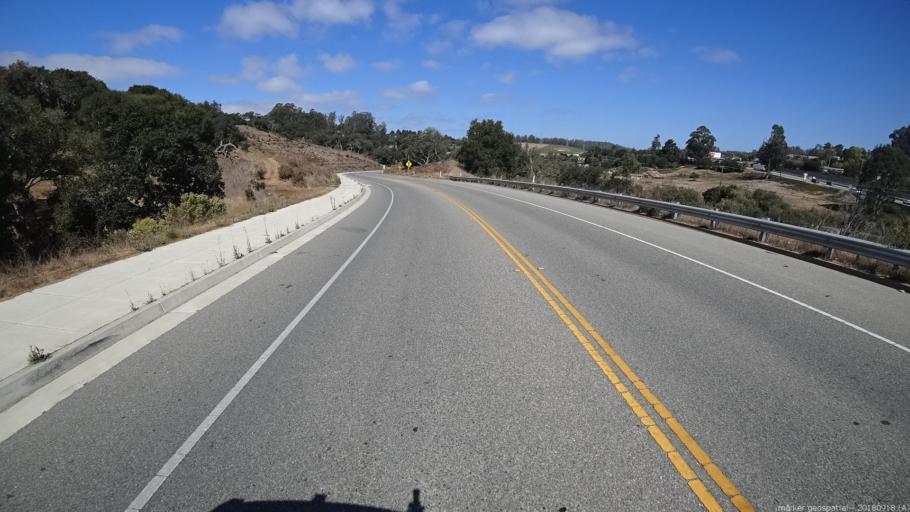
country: US
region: California
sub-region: Monterey County
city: Prunedale
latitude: 36.7724
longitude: -121.6707
